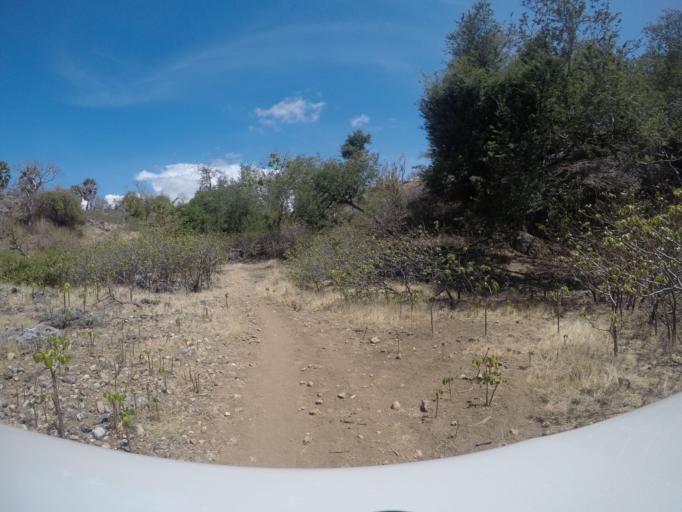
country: TL
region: Baucau
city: Baucau
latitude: -8.4321
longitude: 126.4421
